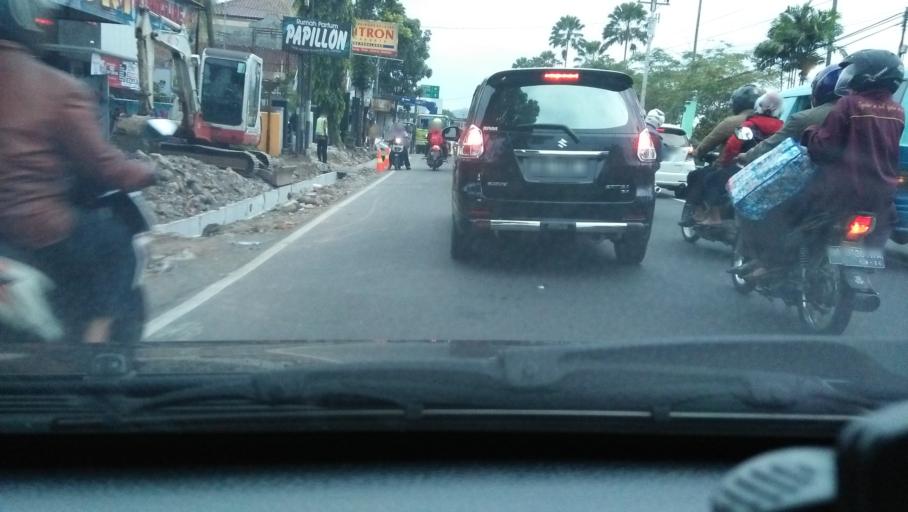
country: ID
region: Central Java
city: Magelang
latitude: -7.4613
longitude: 110.2225
